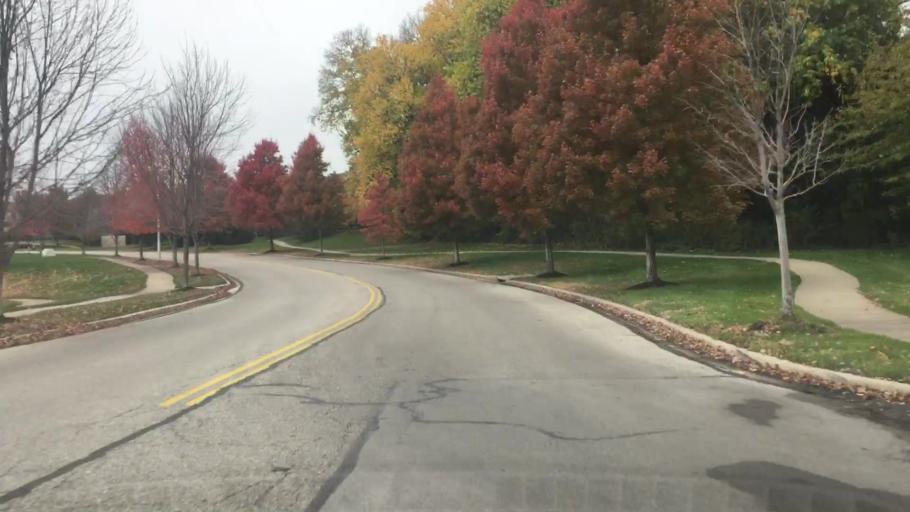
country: US
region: Kansas
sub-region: Johnson County
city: Lenexa
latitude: 38.9171
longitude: -94.7513
